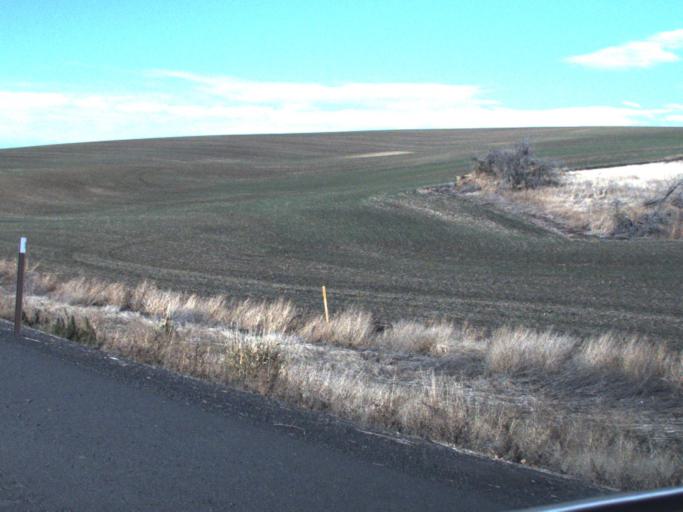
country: US
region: Washington
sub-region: Whitman County
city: Pullman
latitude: 46.7281
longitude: -117.1118
